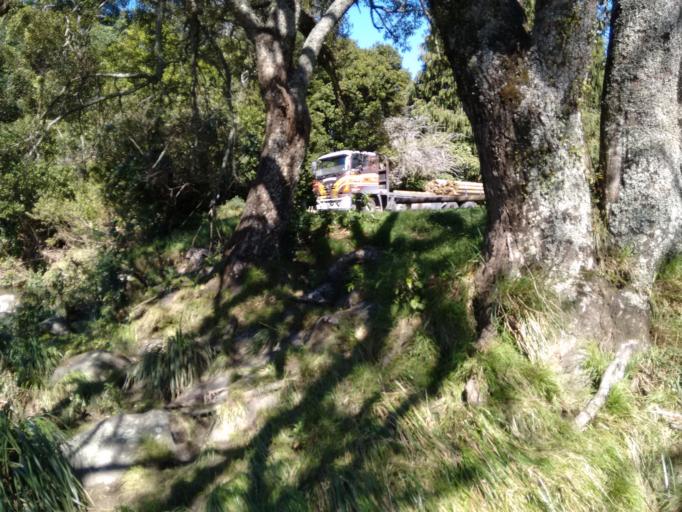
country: NZ
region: Taranaki
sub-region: New Plymouth District
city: New Plymouth
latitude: -39.1032
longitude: 174.1162
